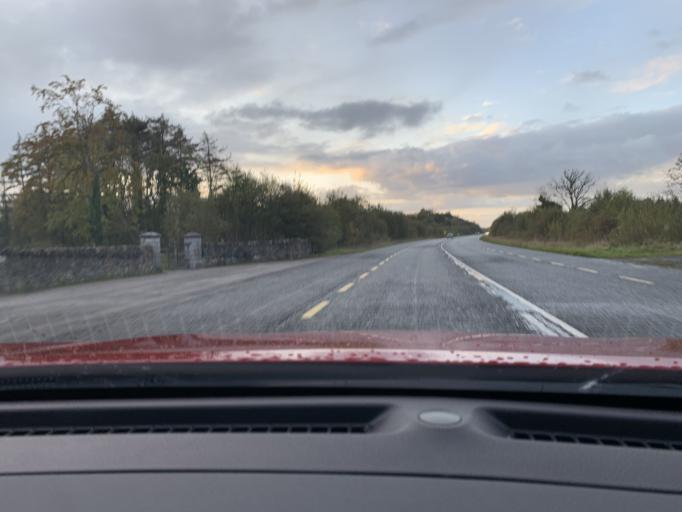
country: IE
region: Connaught
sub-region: County Leitrim
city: Carrick-on-Shannon
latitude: 53.9500
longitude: -8.1483
